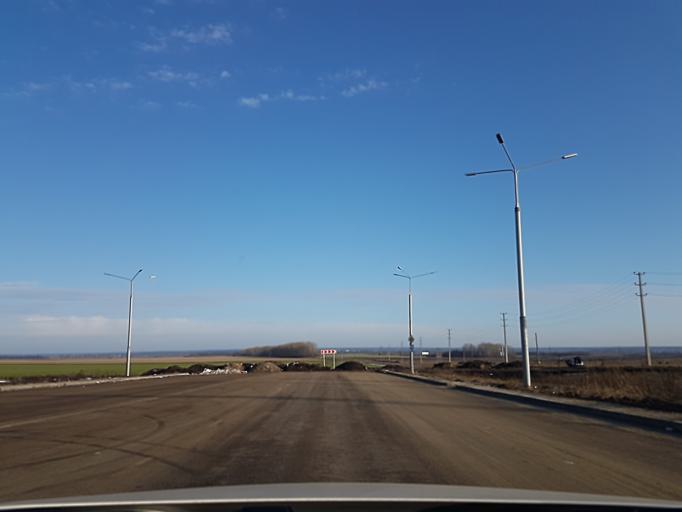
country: RU
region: Tambov
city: Donskoye
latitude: 52.7863
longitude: 41.4246
